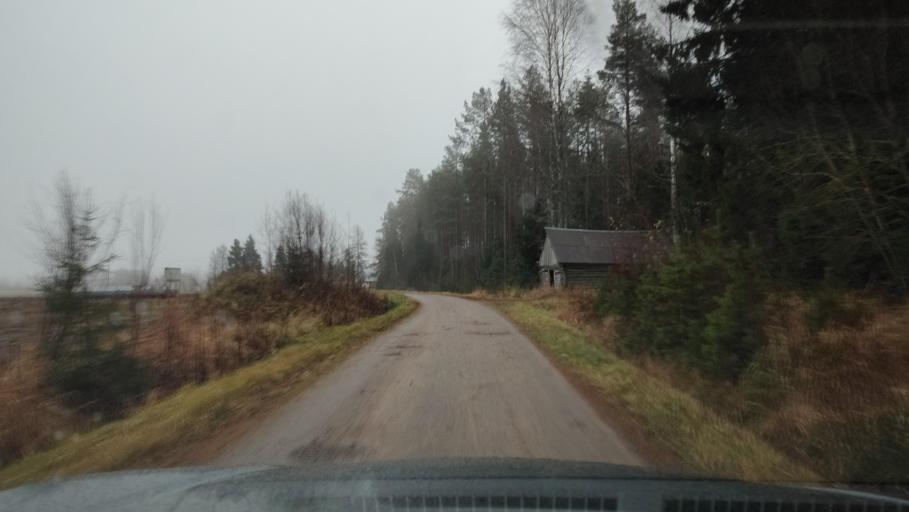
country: FI
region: Southern Ostrobothnia
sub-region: Suupohja
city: Karijoki
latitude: 62.1850
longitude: 21.7794
